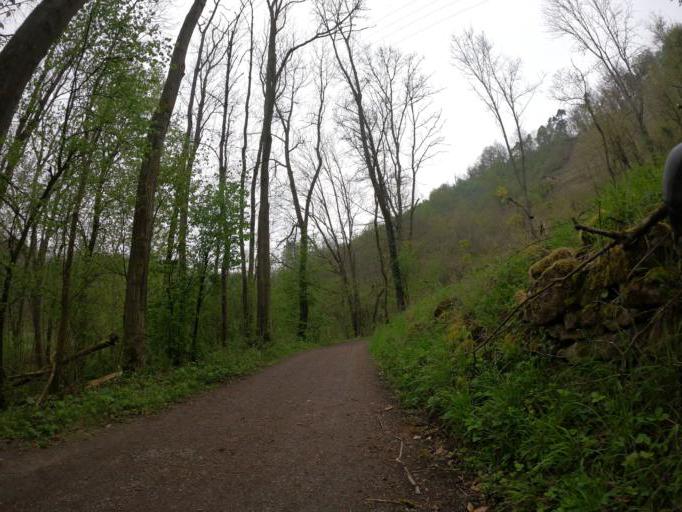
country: DE
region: Baden-Wuerttemberg
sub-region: Regierungsbezirk Stuttgart
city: Markgroningen
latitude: 48.9158
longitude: 9.0858
